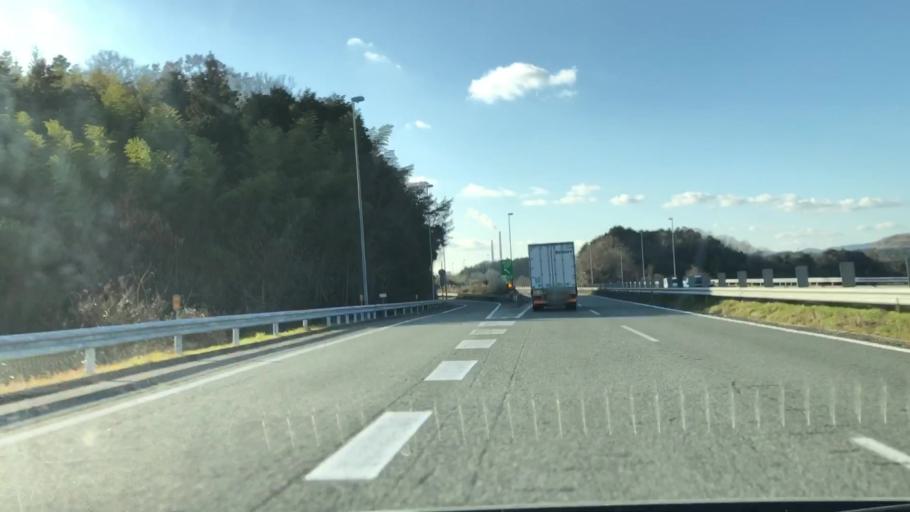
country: JP
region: Yamaguchi
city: Ogori-shimogo
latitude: 34.1705
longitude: 131.2495
